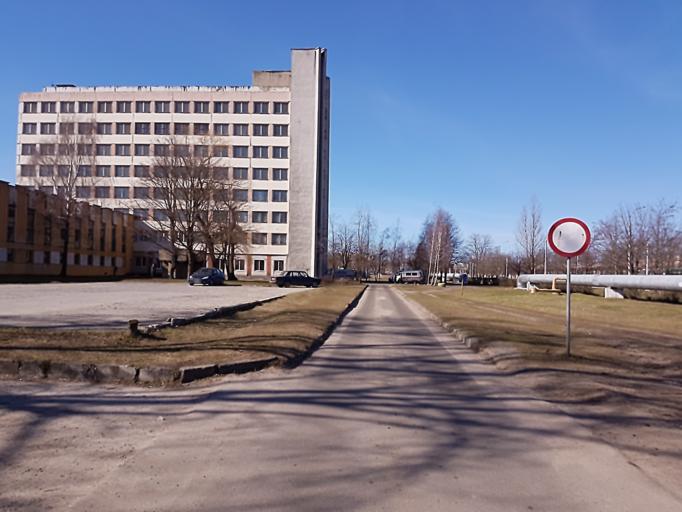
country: BY
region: Mogilev
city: Babruysk
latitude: 53.1804
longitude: 29.2065
